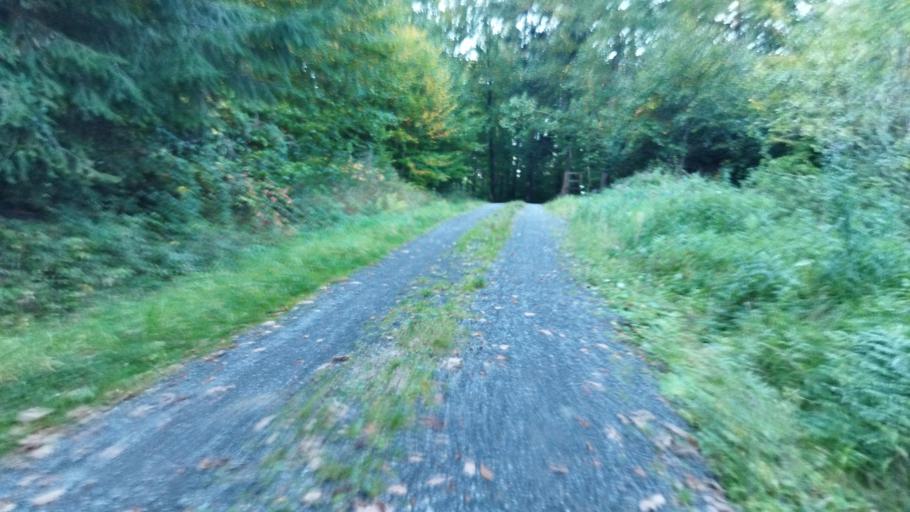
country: DE
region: Baden-Wuerttemberg
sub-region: Regierungsbezirk Stuttgart
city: Freudental
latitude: 49.0119
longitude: 9.0321
